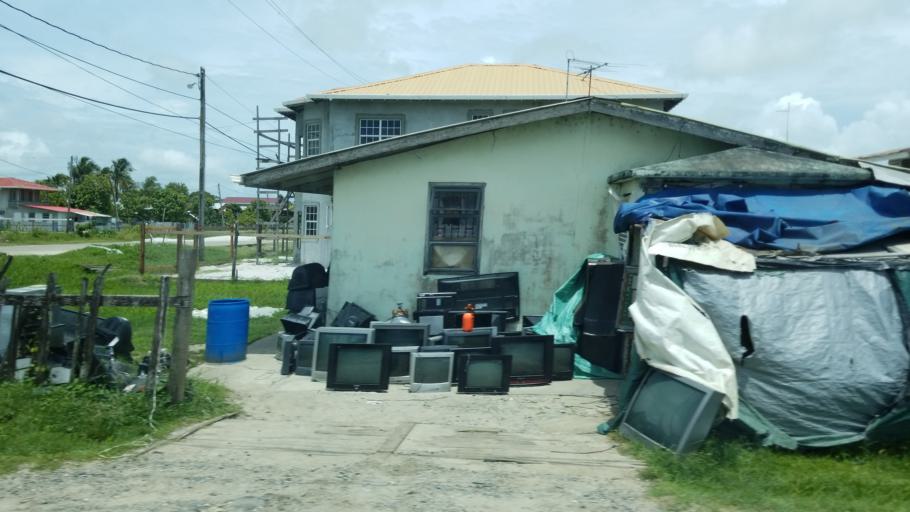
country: GY
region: Demerara-Mahaica
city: Georgetown
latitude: 6.8086
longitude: -58.1216
